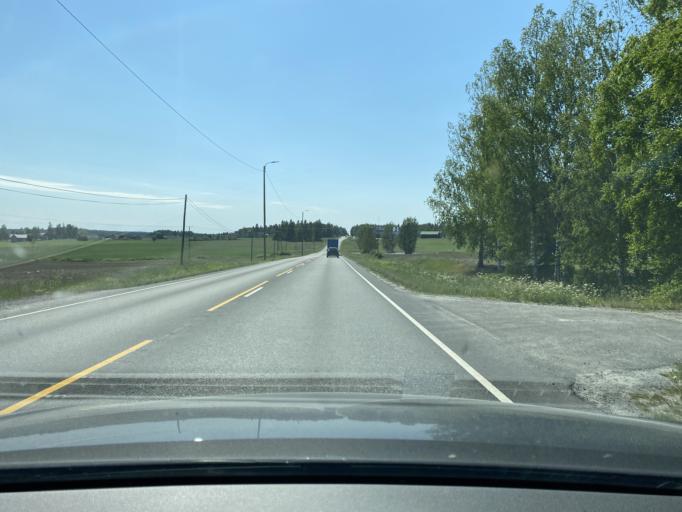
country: FI
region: Pirkanmaa
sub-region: Lounais-Pirkanmaa
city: Mouhijaervi
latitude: 61.3536
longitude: 23.0747
